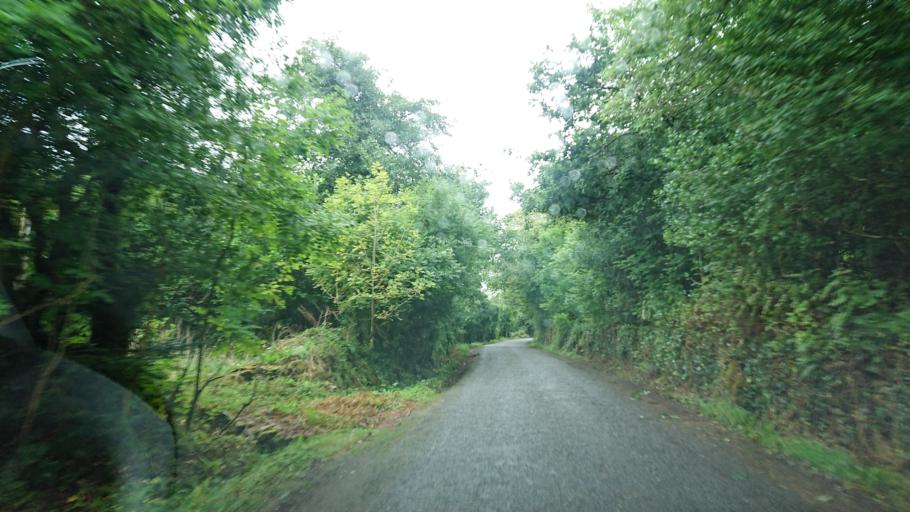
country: IE
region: Munster
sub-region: Ciarrai
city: Cahersiveen
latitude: 52.0193
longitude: -10.0978
